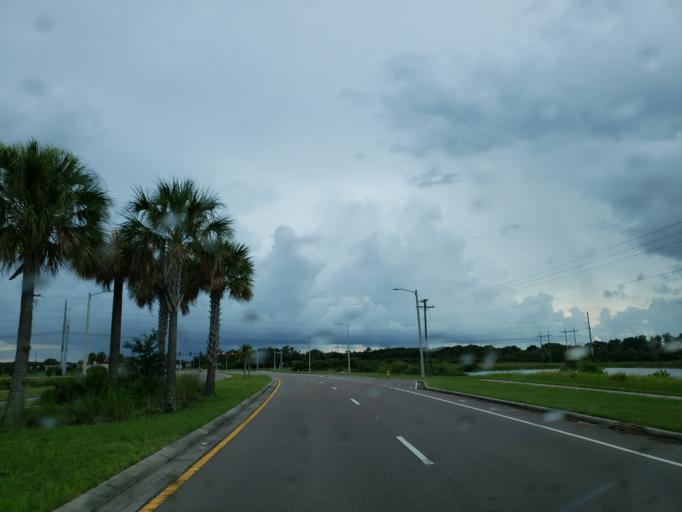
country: US
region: Florida
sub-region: Hillsborough County
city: Ruskin
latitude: 27.7217
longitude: -82.3938
